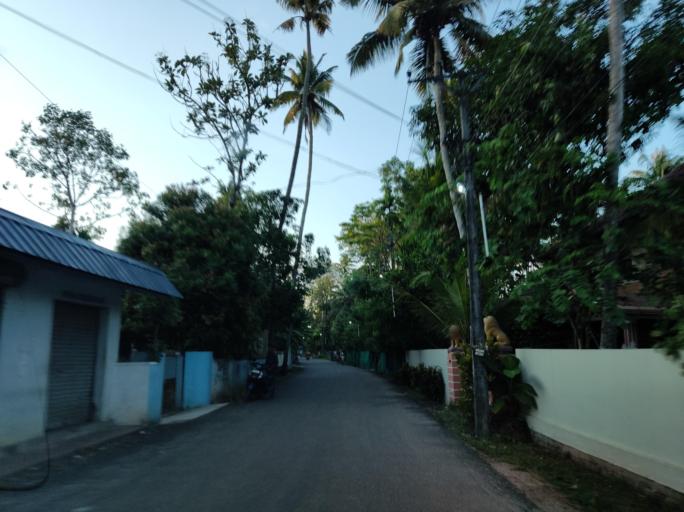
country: IN
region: Kerala
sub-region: Alappuzha
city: Vayalar
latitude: 9.7159
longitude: 76.2973
